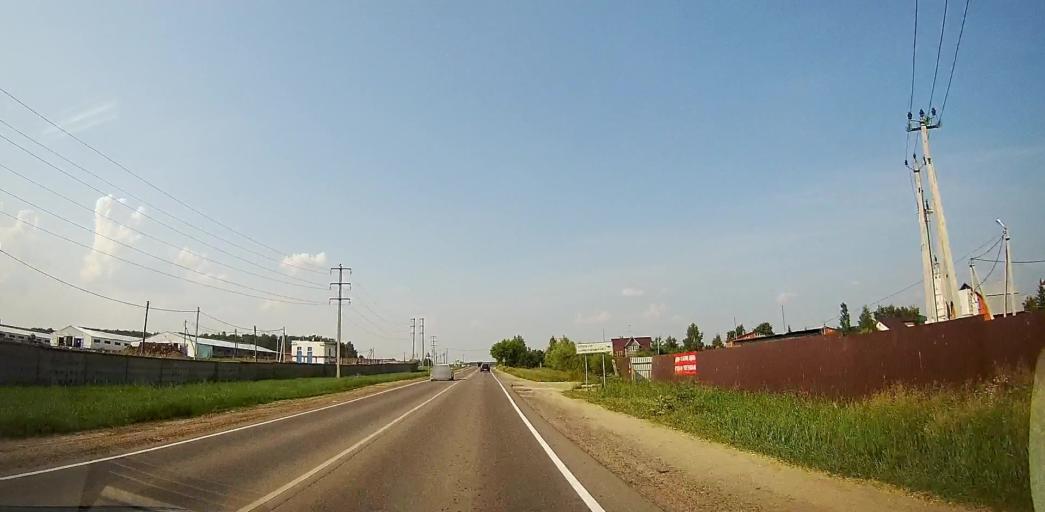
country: RU
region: Moskovskaya
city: Barybino
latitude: 55.3030
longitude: 37.9104
